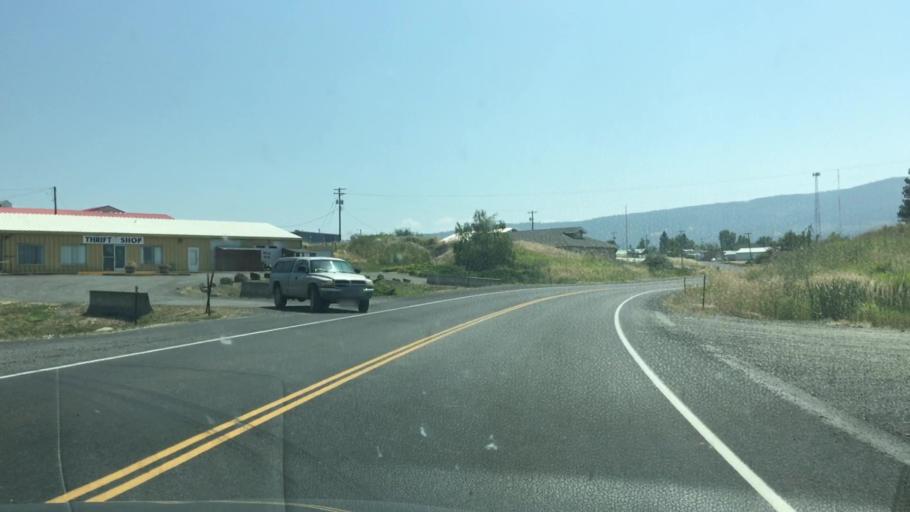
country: US
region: Idaho
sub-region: Idaho County
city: Grangeville
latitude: 45.9350
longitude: -116.1337
